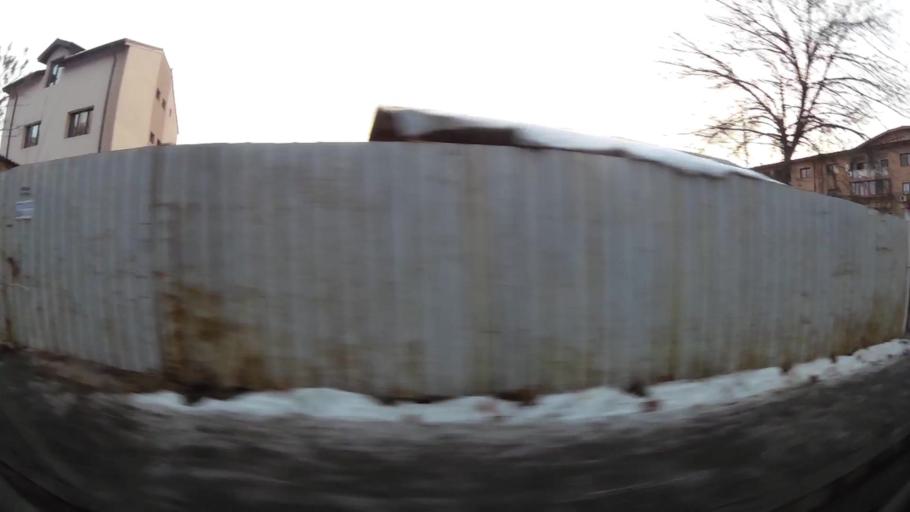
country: RO
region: Ilfov
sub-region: Comuna Fundeni-Dobroesti
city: Fundeni
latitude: 44.4636
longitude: 26.1408
